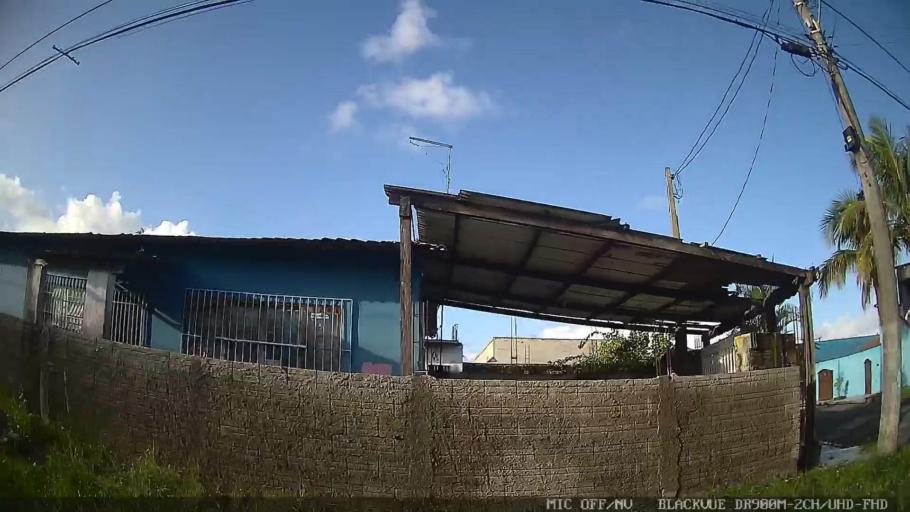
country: BR
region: Sao Paulo
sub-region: Itanhaem
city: Itanhaem
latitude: -24.1398
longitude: -46.7147
